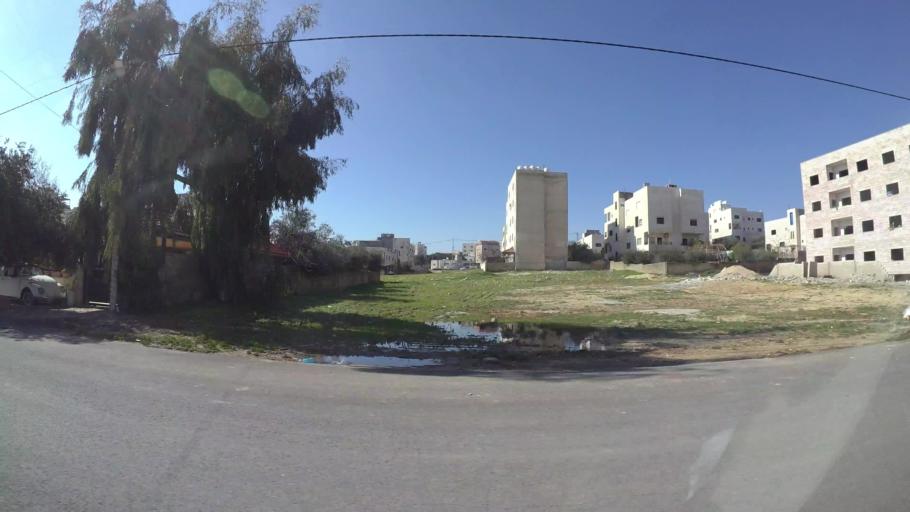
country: JO
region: Amman
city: Al Bunayyat ash Shamaliyah
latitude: 31.9062
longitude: 35.8893
